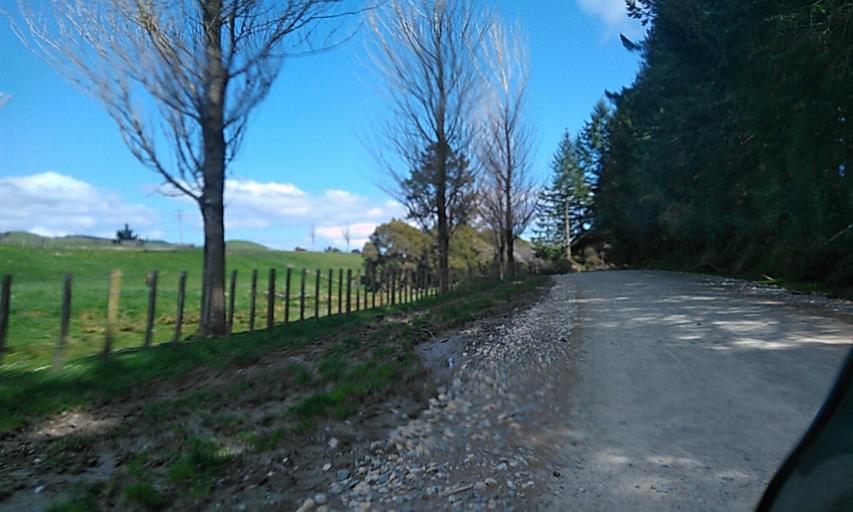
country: NZ
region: Gisborne
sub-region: Gisborne District
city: Gisborne
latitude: -38.2157
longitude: 178.0706
